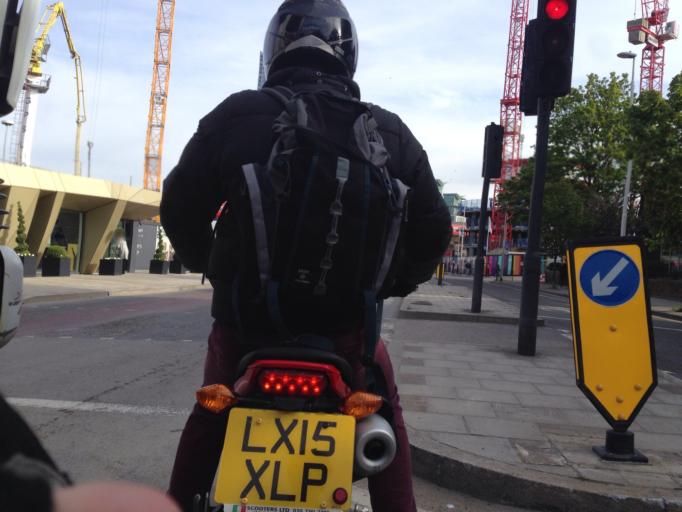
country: GB
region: England
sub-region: Greater London
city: City of Westminster
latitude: 51.4808
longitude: -0.1278
